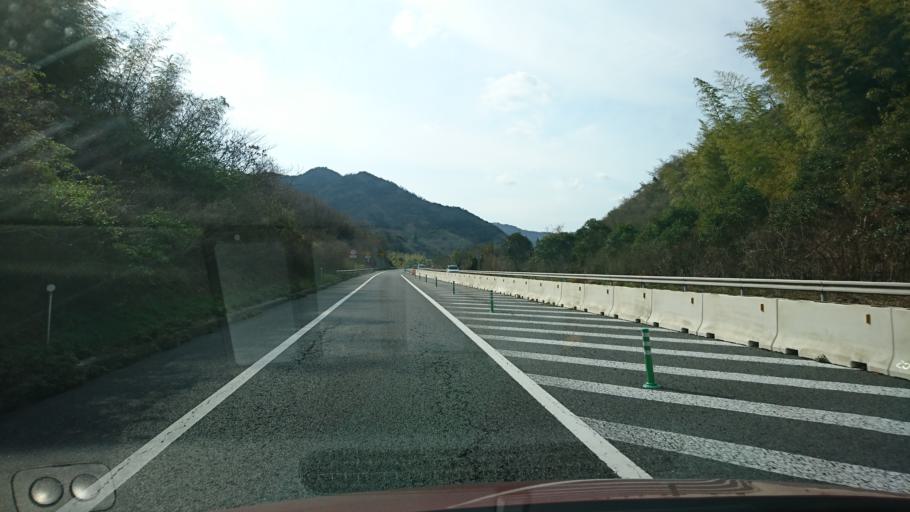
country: JP
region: Hiroshima
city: Innoshima
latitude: 34.1379
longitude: 133.0538
